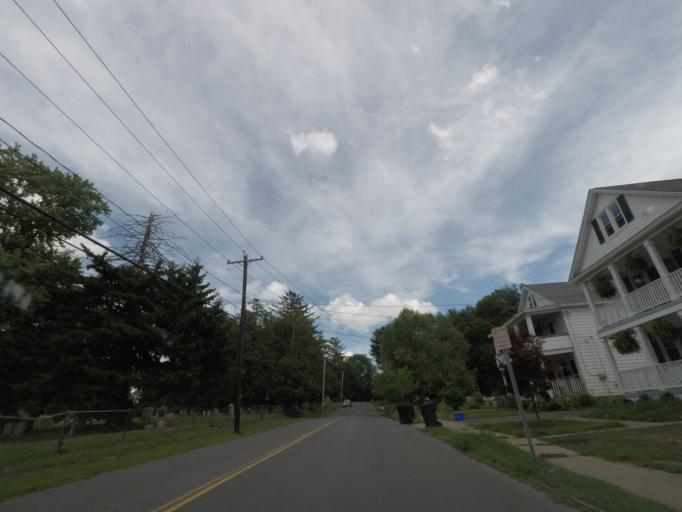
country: US
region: New York
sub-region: Rensselaer County
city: Wynantskill
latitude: 42.7171
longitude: -73.6646
